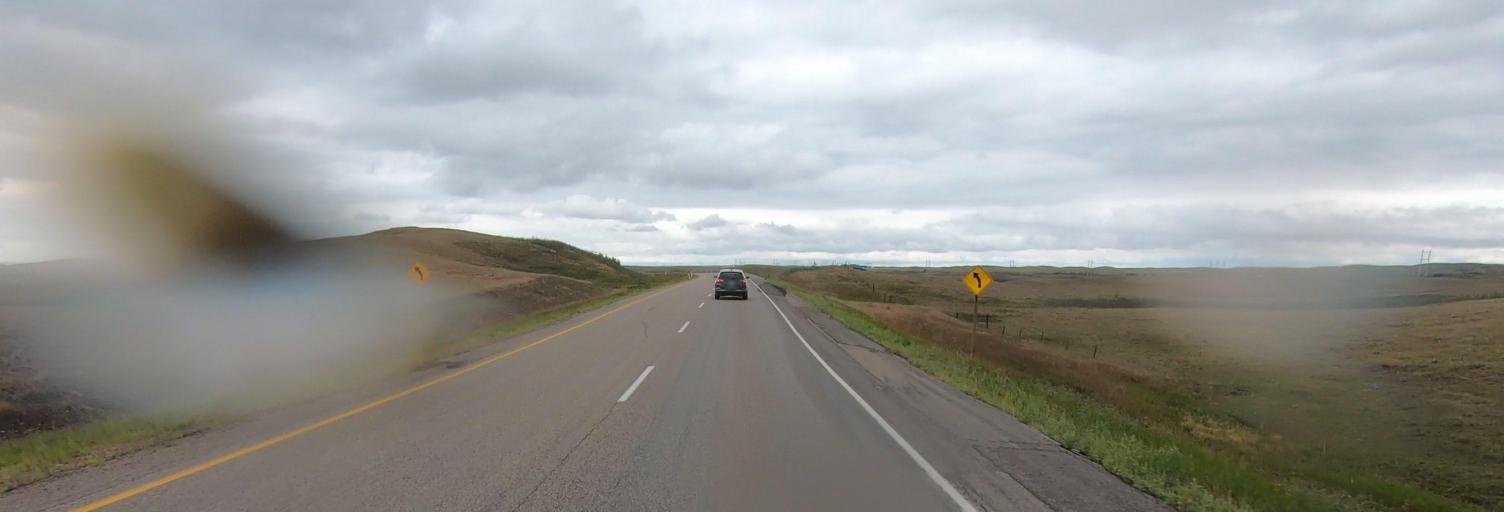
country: CA
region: Saskatchewan
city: Gravelbourg
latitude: 50.4636
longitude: -106.4978
